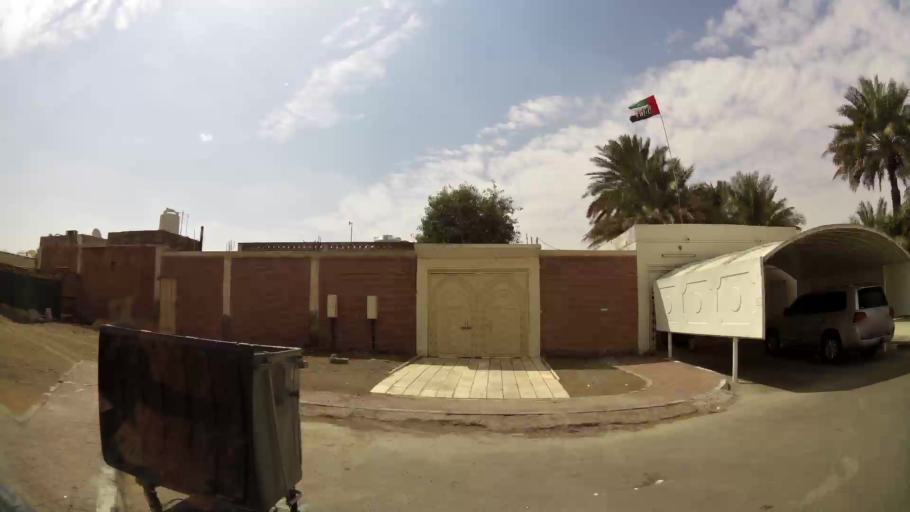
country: AE
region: Abu Dhabi
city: Al Ain
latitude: 24.1990
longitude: 55.7870
